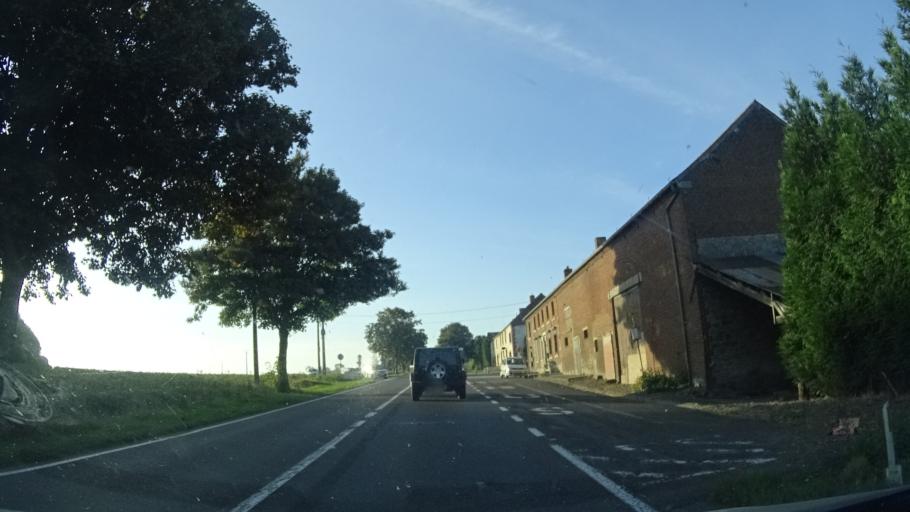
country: BE
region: Wallonia
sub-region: Province du Hainaut
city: Beaumont
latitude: 50.2712
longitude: 4.2131
